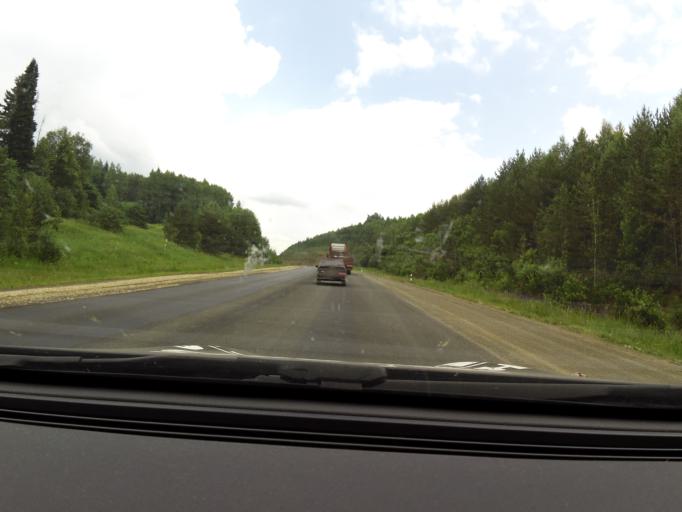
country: RU
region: Sverdlovsk
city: Ufimskiy
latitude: 56.7823
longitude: 58.3013
